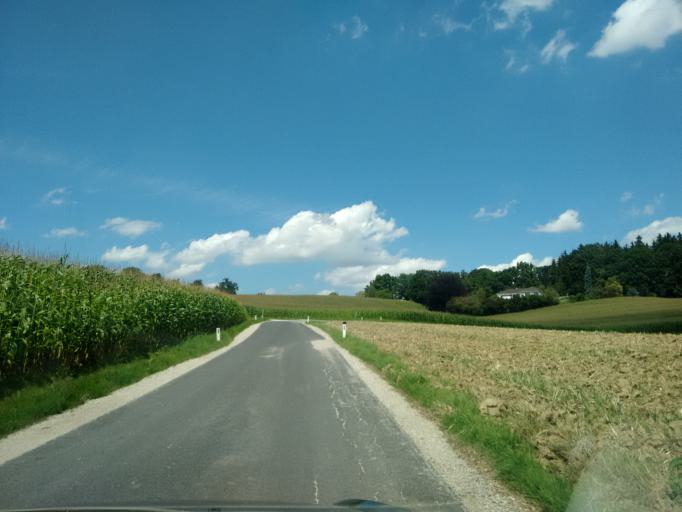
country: AT
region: Upper Austria
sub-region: Wels-Land
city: Gunskirchen
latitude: 48.1802
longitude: 13.9696
